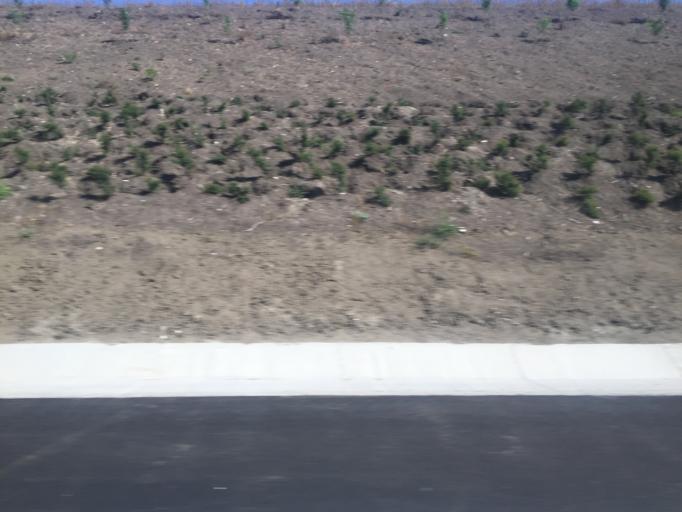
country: TR
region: Bursa
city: Mahmudiye
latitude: 40.2571
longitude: 28.7217
